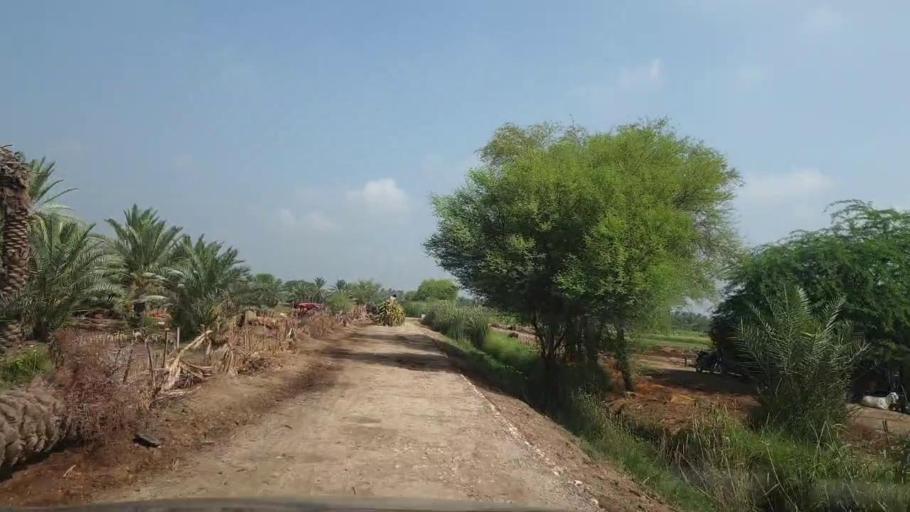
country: PK
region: Sindh
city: Pir jo Goth
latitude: 27.5986
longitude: 68.6935
